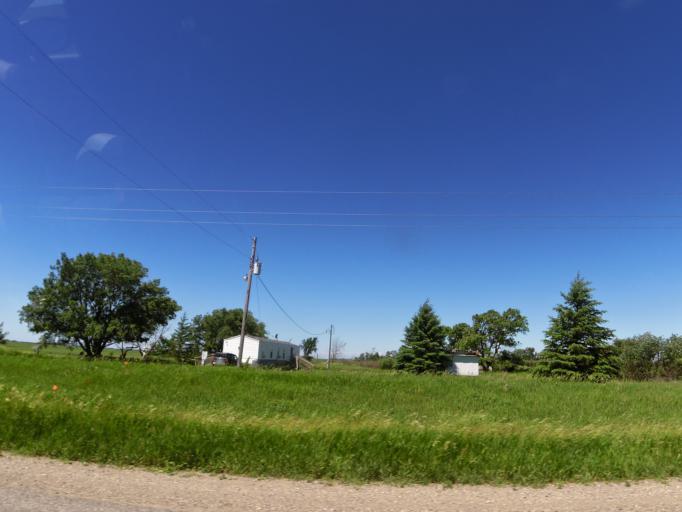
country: US
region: Minnesota
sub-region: Mahnomen County
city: Mahnomen
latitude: 47.2859
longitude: -95.9334
